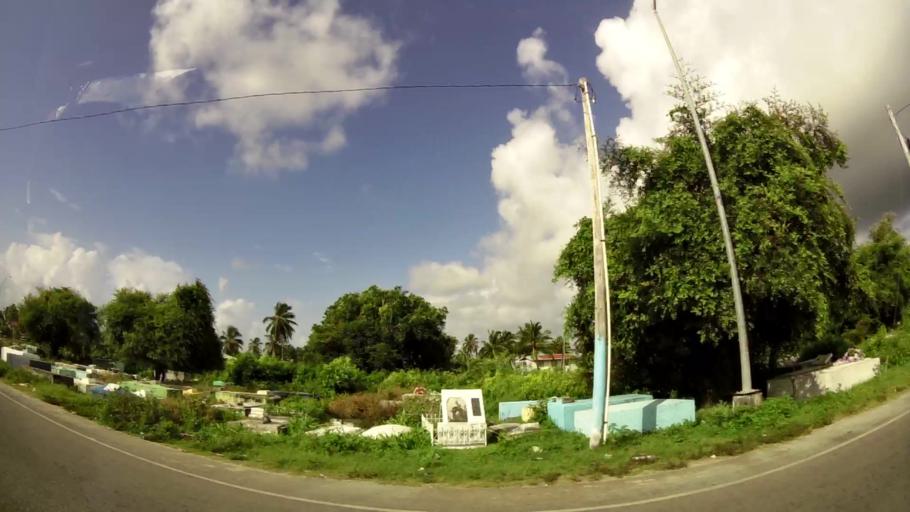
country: GY
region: Demerara-Mahaica
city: Mahaica Village
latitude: 6.7743
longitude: -57.9991
